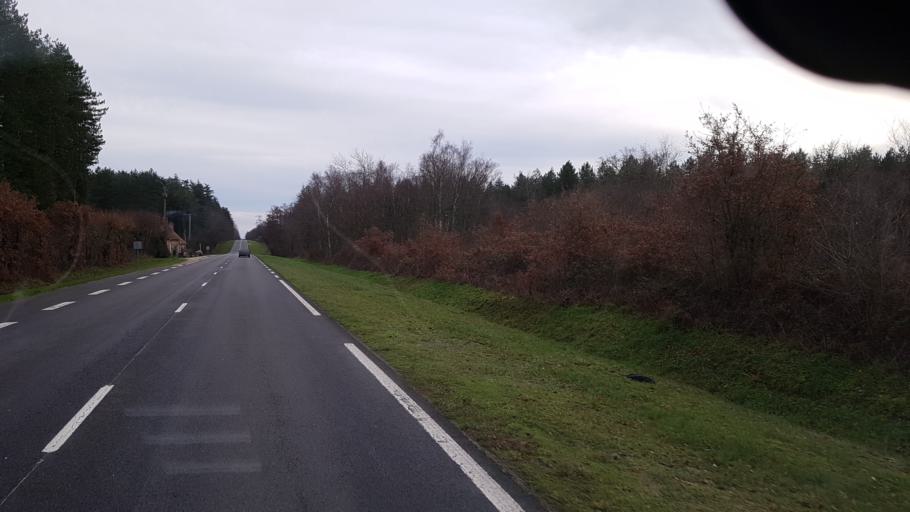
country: FR
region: Centre
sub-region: Departement du Loir-et-Cher
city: Lamotte-Beuvron
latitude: 47.6314
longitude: 2.0044
